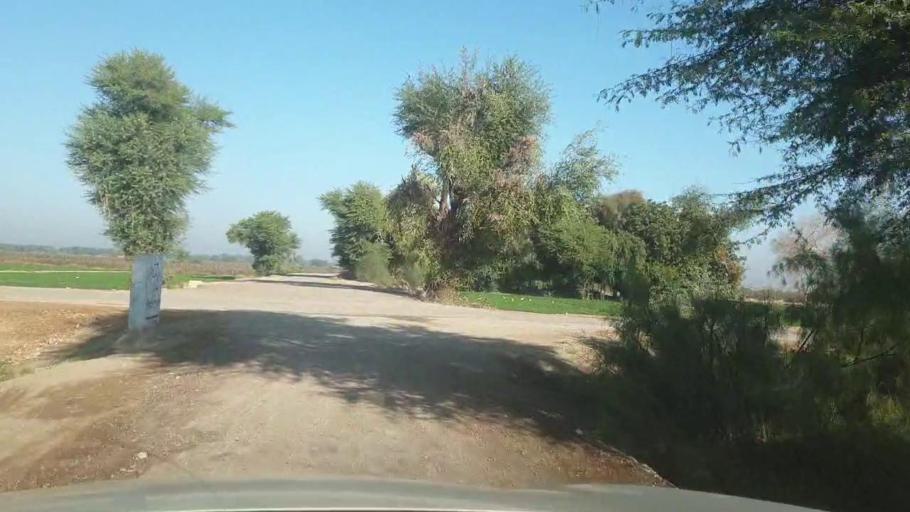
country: PK
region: Sindh
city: Bhan
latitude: 26.5410
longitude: 67.6892
